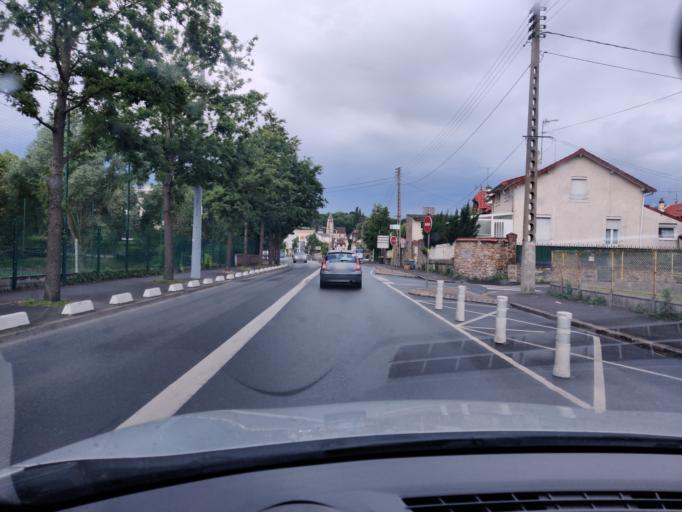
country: FR
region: Ile-de-France
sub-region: Departement de l'Essonne
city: Juvisy-sur-Orge
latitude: 48.6726
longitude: 2.3802
